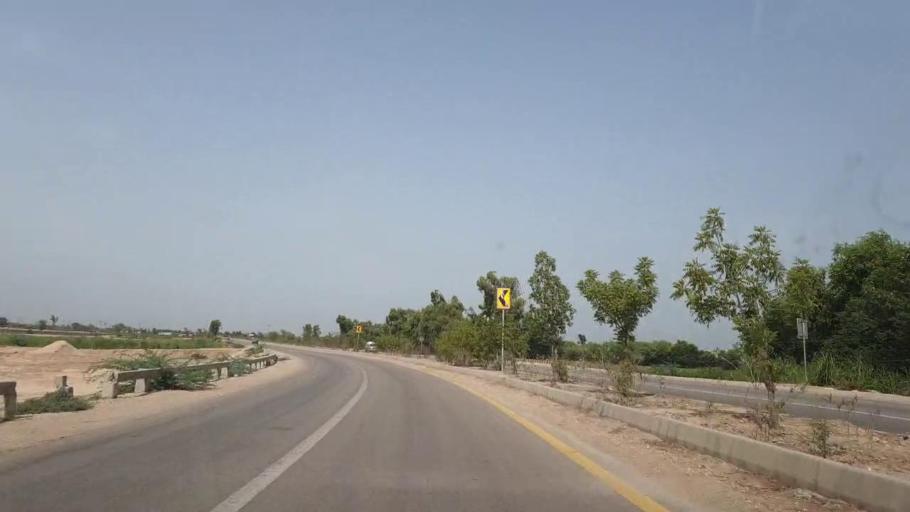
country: PK
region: Sindh
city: Sakrand
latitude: 26.1978
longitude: 68.3083
